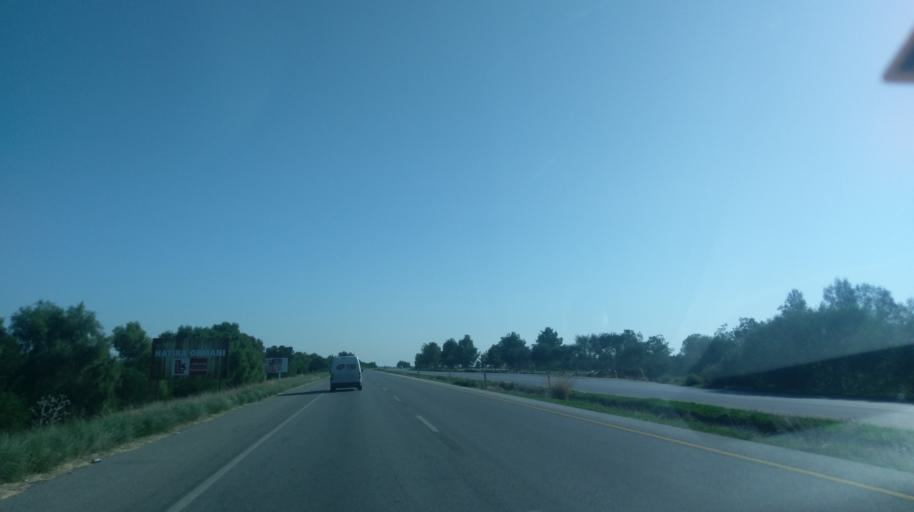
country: CY
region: Ammochostos
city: Lefkonoiko
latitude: 35.1860
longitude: 33.6576
